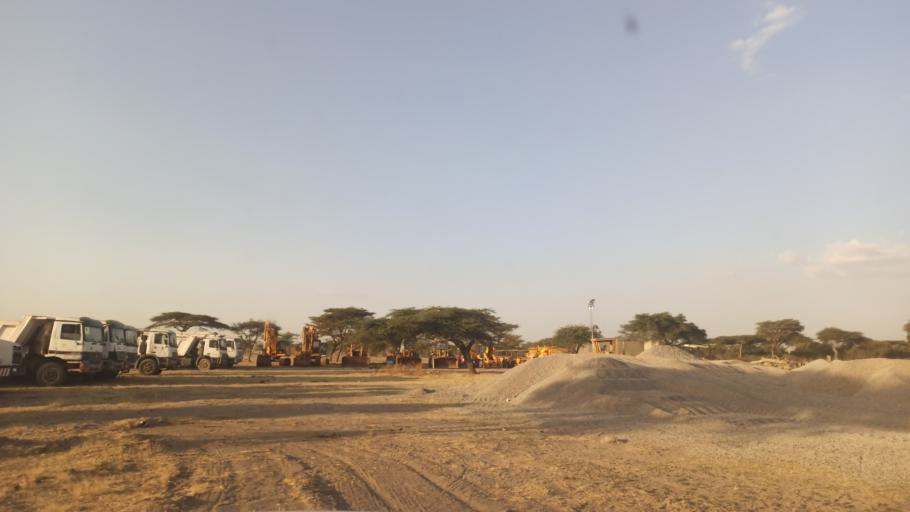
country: ET
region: Oromiya
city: Ziway
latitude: 7.6983
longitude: 38.6560
